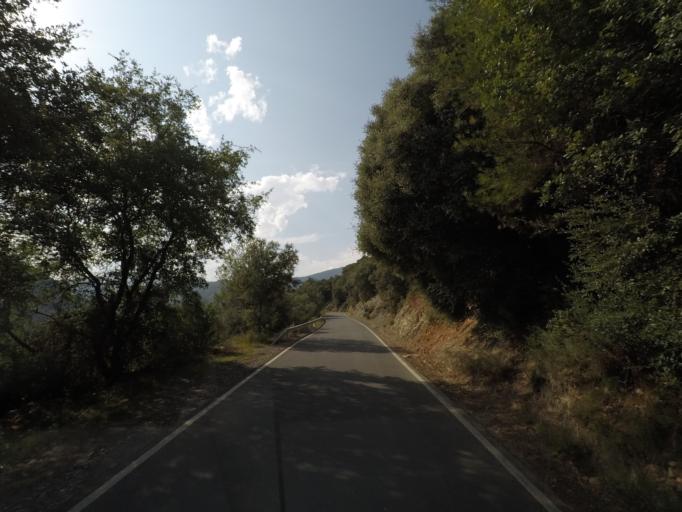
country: ES
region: Aragon
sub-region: Provincia de Huesca
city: Laspuna
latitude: 42.5036
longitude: 0.1364
